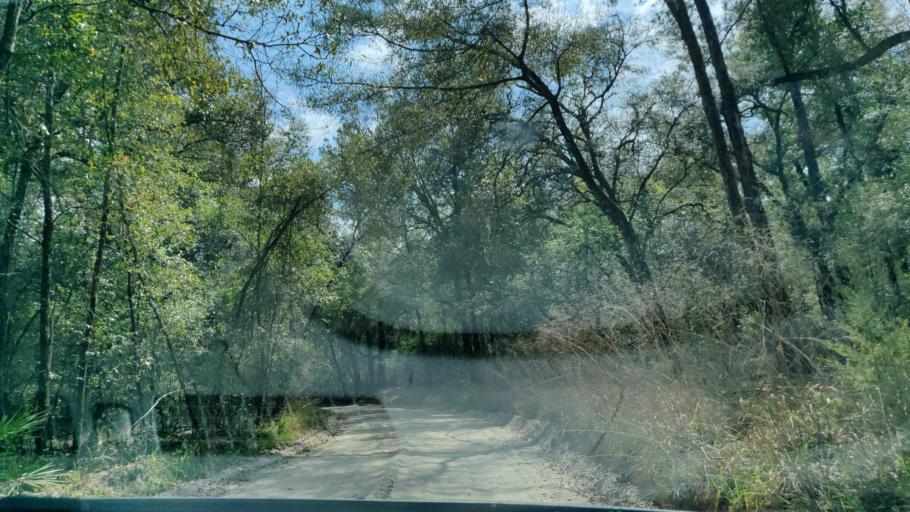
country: US
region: Florida
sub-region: Clay County
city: Middleburg
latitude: 30.1552
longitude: -81.9341
